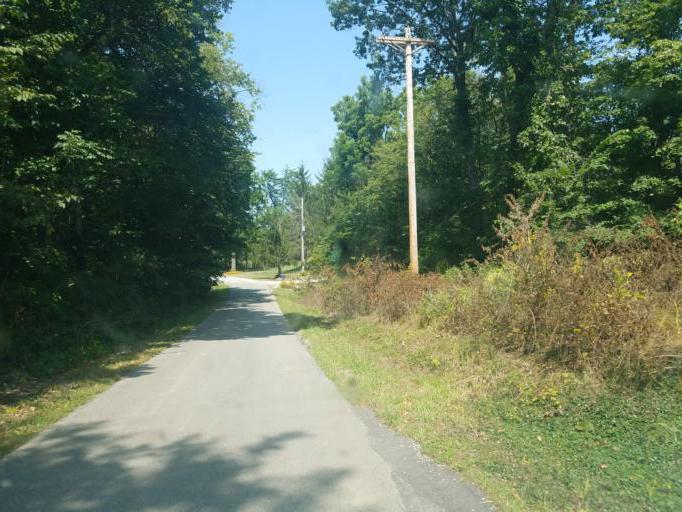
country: US
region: Ohio
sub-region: Crawford County
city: Bucyrus
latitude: 40.7981
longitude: -83.1112
